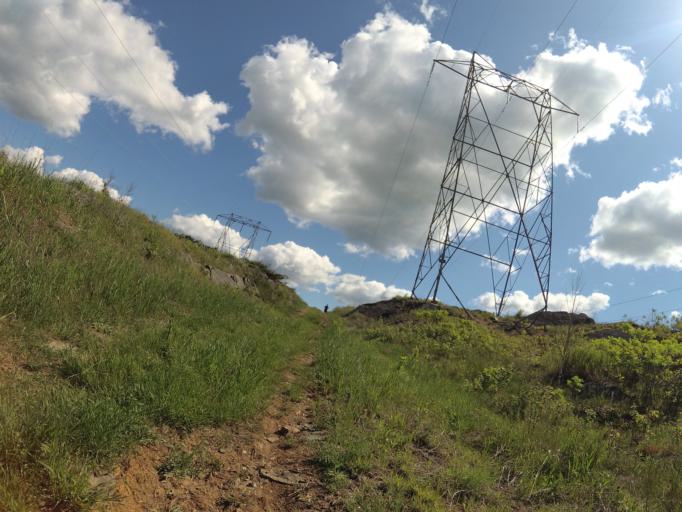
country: CA
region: Ontario
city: Renfrew
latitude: 45.0444
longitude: -76.7688
